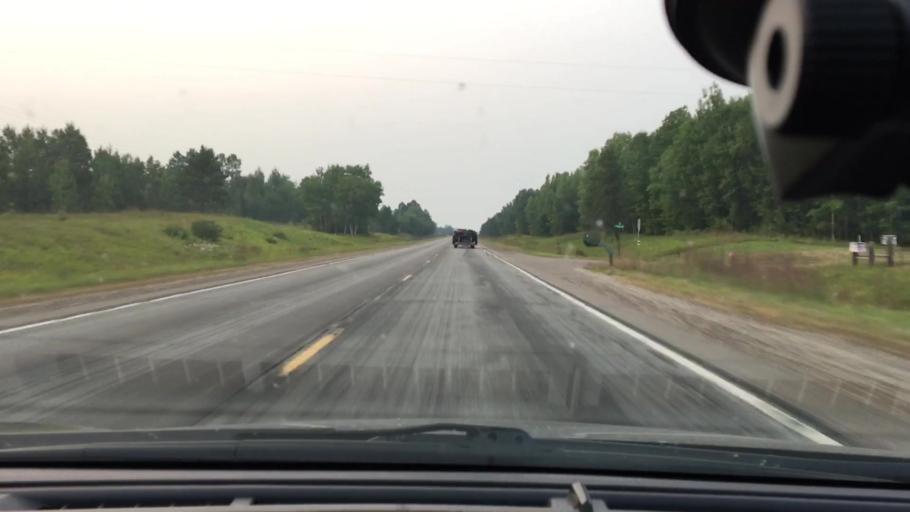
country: US
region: Minnesota
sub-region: Crow Wing County
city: Cross Lake
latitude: 46.6784
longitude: -93.9528
